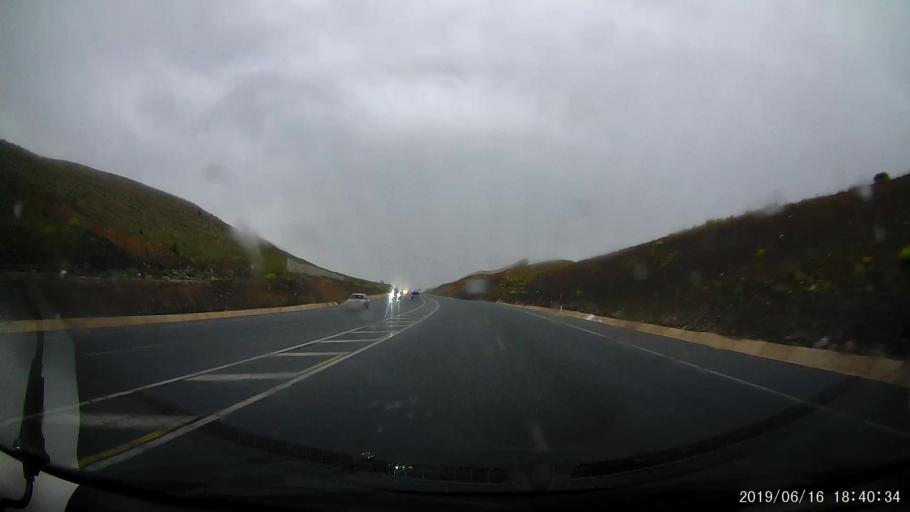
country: TR
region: Erzincan
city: Catalarmut
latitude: 39.8811
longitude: 39.1438
